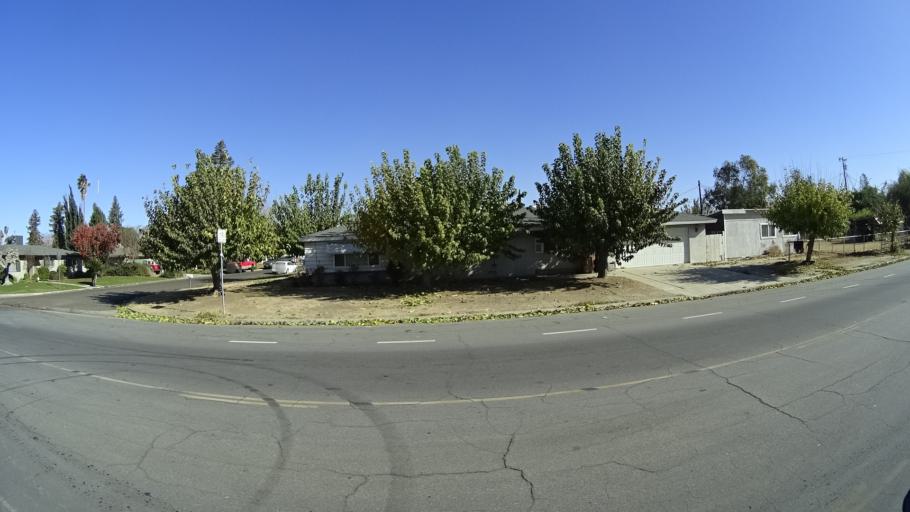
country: US
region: California
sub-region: Kern County
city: Greenfield
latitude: 35.3045
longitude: -119.0479
